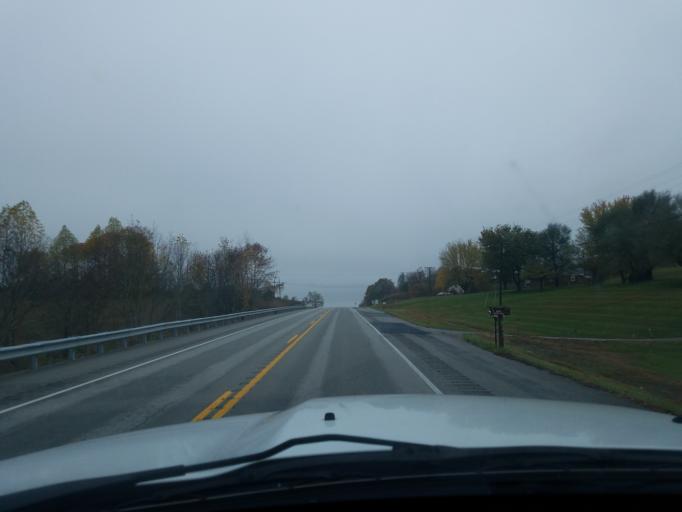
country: US
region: Kentucky
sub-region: Taylor County
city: Campbellsville
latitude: 37.3855
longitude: -85.4181
